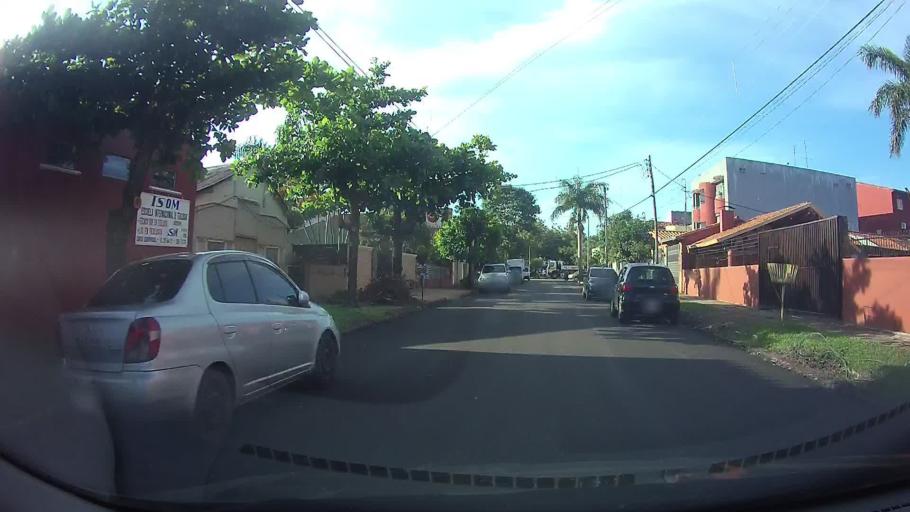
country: PY
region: Central
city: San Lorenzo
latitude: -25.2639
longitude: -57.5015
